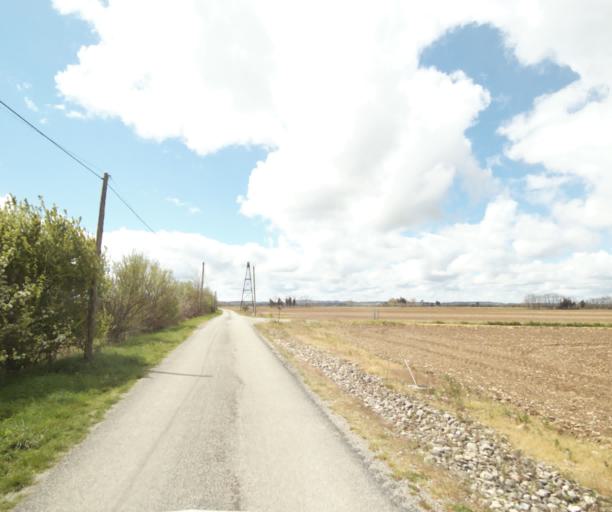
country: FR
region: Midi-Pyrenees
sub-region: Departement de l'Ariege
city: Saverdun
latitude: 43.2514
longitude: 1.6091
